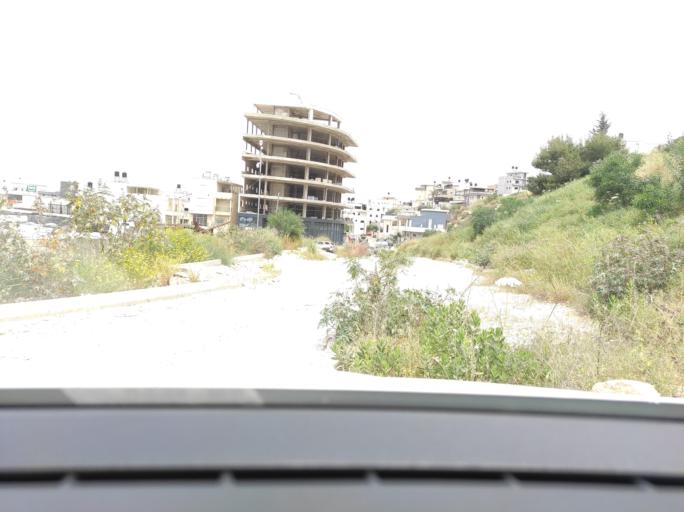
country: IL
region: Central District
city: Kafr Qasim
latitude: 32.1139
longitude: 34.9651
